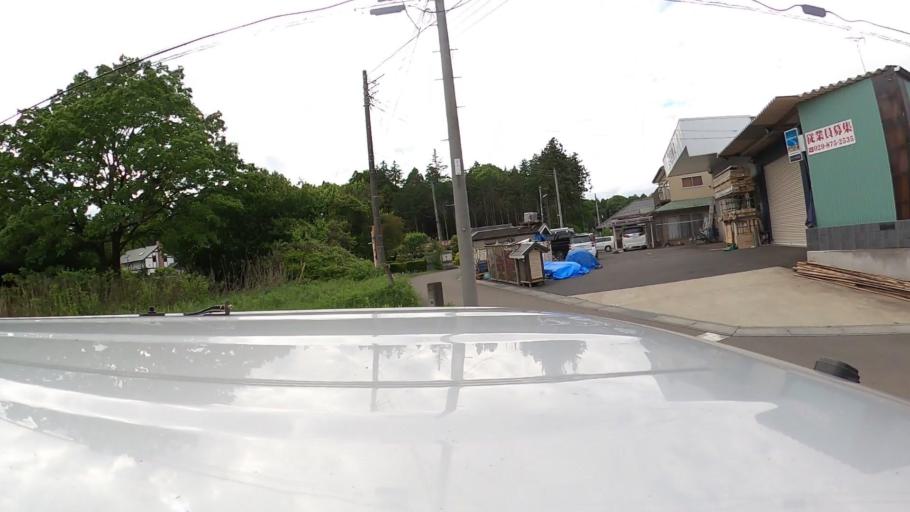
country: JP
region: Ibaraki
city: Ami
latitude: 35.9751
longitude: 140.2355
